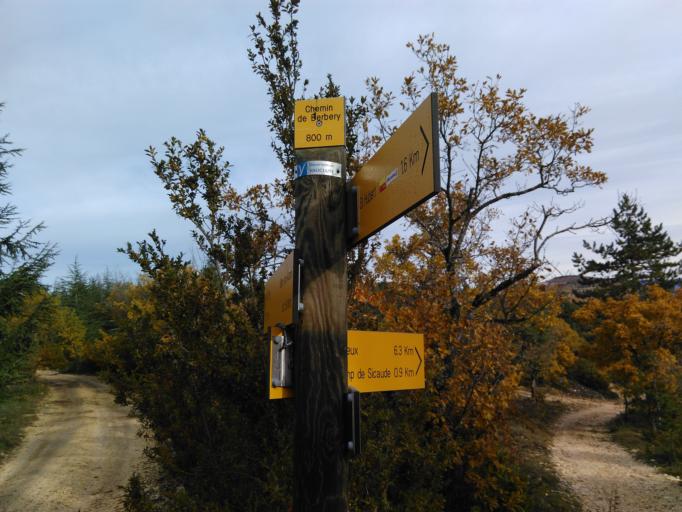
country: FR
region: Provence-Alpes-Cote d'Azur
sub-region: Departement du Vaucluse
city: Villes-sur-Auzon
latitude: 44.0391
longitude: 5.3217
